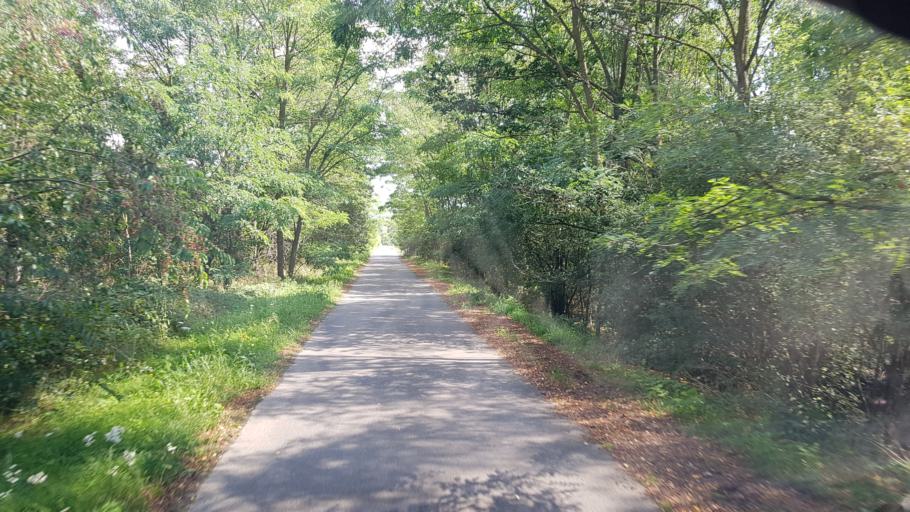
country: DE
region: Brandenburg
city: Calau
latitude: 51.7770
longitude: 13.9483
